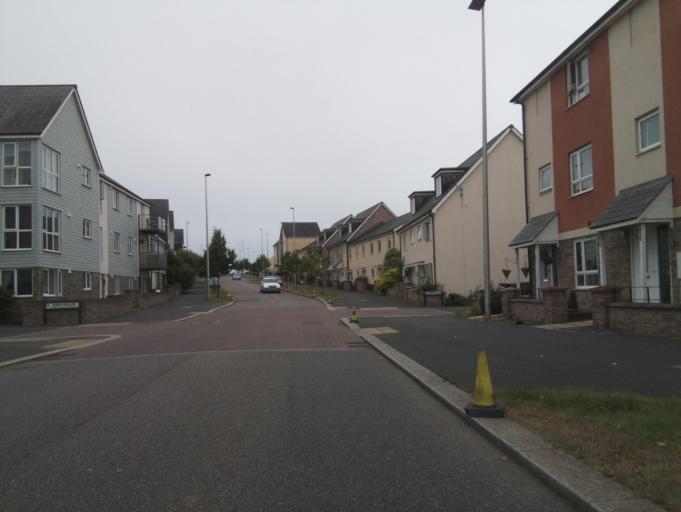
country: GB
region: England
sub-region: Devon
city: Topsham
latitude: 50.7461
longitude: -3.4161
